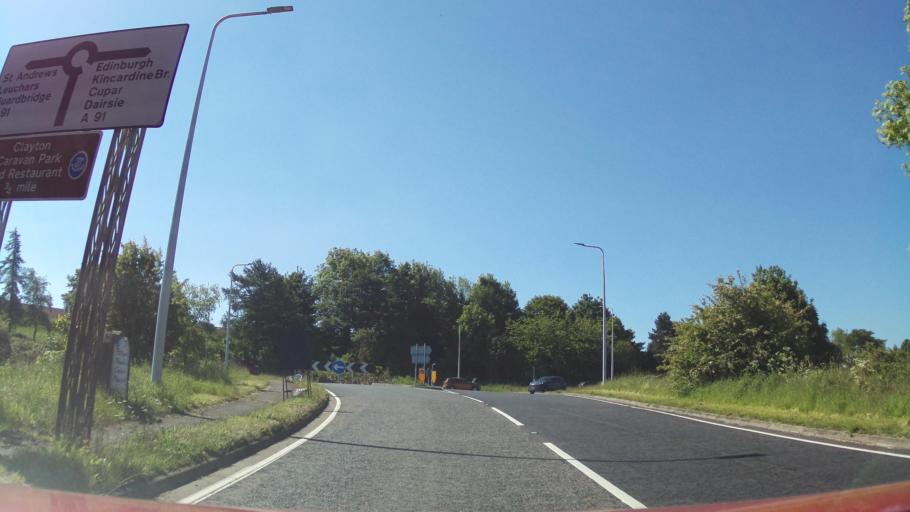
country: GB
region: Scotland
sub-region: Fife
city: Balmullo
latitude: 56.3492
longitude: -2.9415
